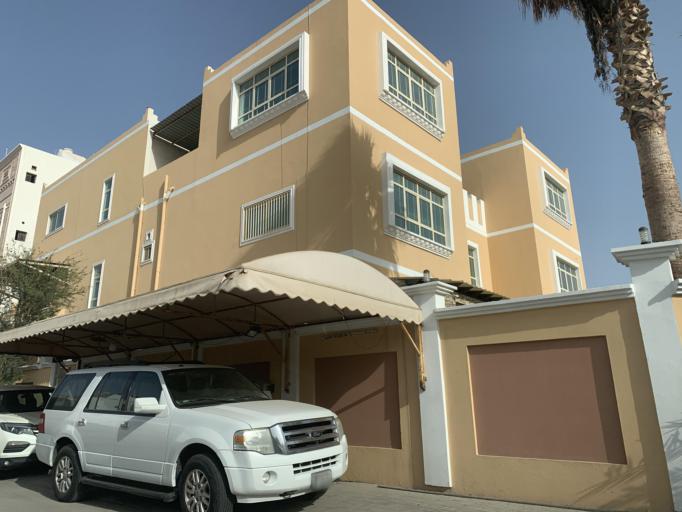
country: BH
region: Northern
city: Ar Rifa'
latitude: 26.1424
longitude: 50.5827
